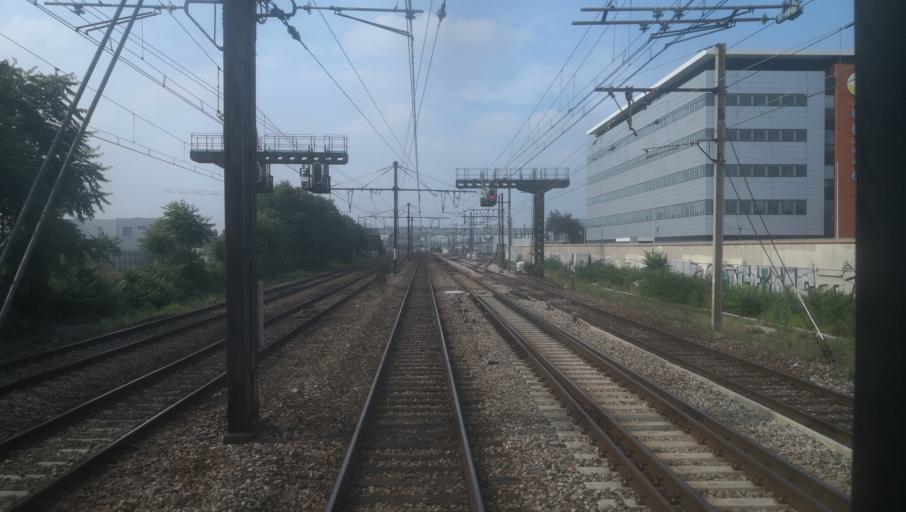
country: FR
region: Ile-de-France
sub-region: Departement du Val-de-Marne
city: Vitry-sur-Seine
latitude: 48.7778
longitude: 2.4101
